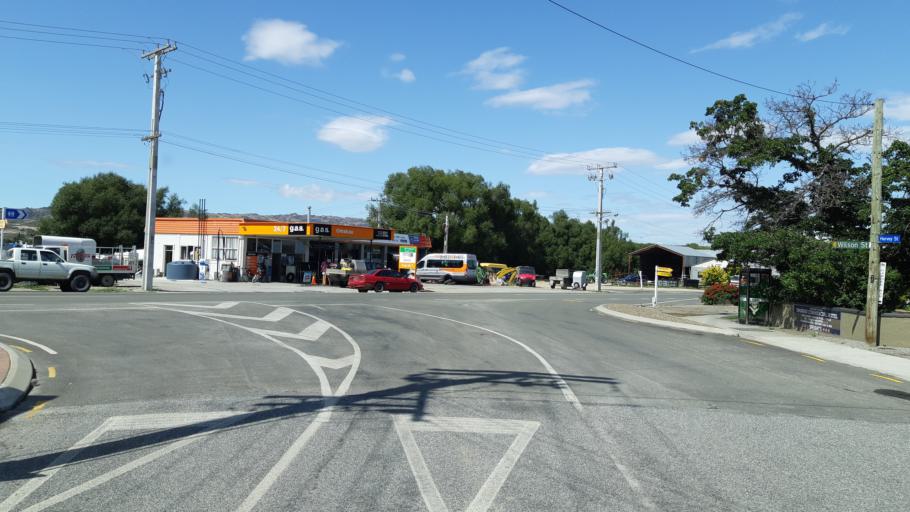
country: NZ
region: Otago
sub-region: Queenstown-Lakes District
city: Wanaka
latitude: -45.0939
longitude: 169.6019
